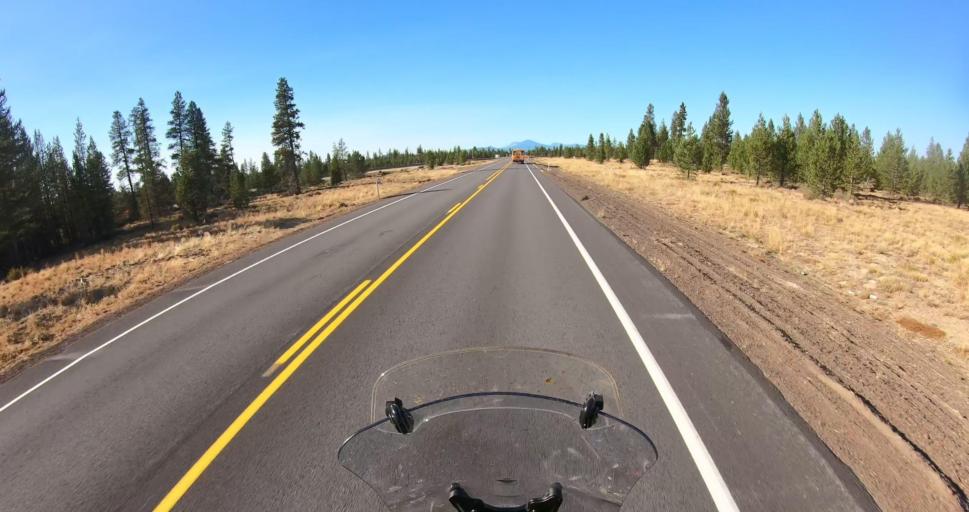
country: US
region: Oregon
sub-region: Deschutes County
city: La Pine
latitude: 43.6042
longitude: -121.4995
